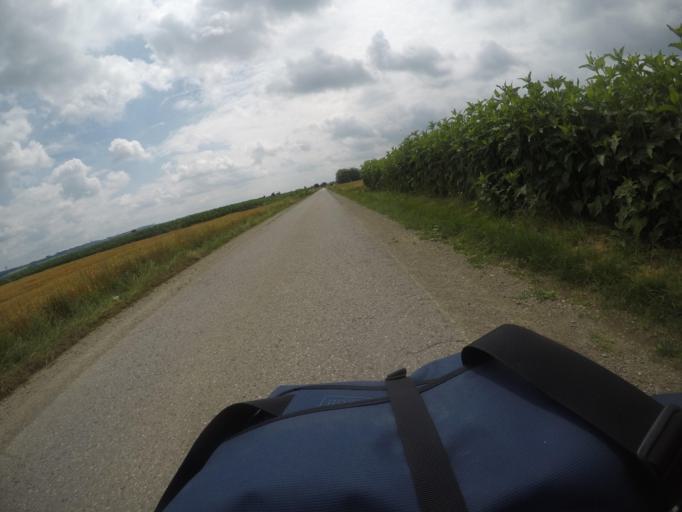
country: DE
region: Bavaria
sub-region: Swabia
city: Fellheim
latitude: 48.0850
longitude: 10.1560
